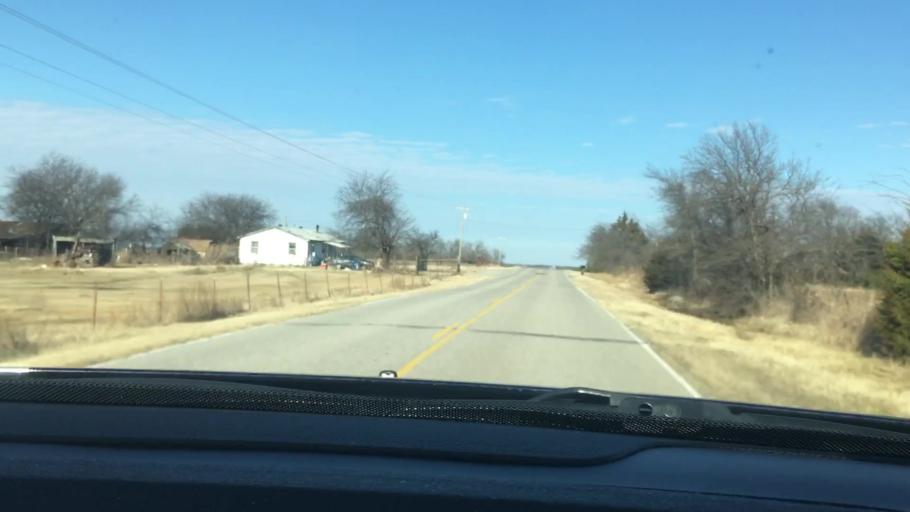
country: US
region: Oklahoma
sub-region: Garvin County
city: Wynnewood
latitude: 34.7049
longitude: -97.1254
